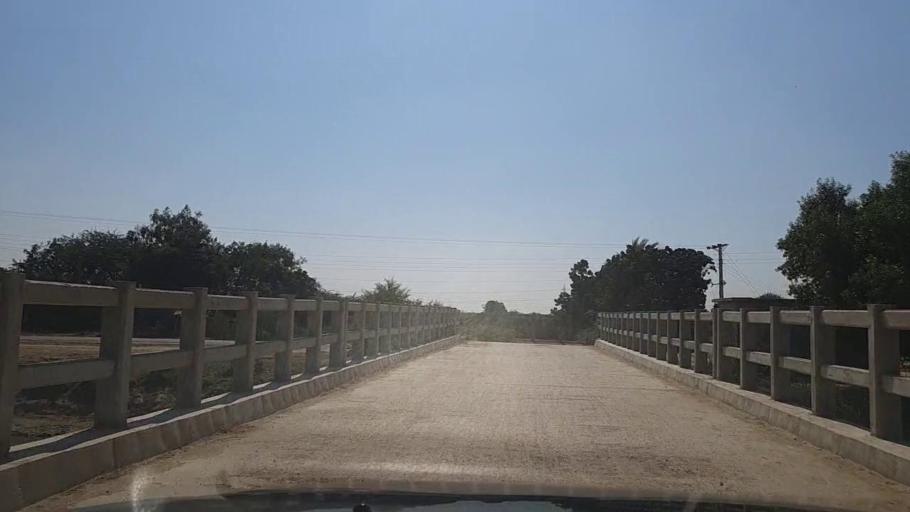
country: PK
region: Sindh
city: Mirpur Sakro
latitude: 24.5745
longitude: 67.7884
